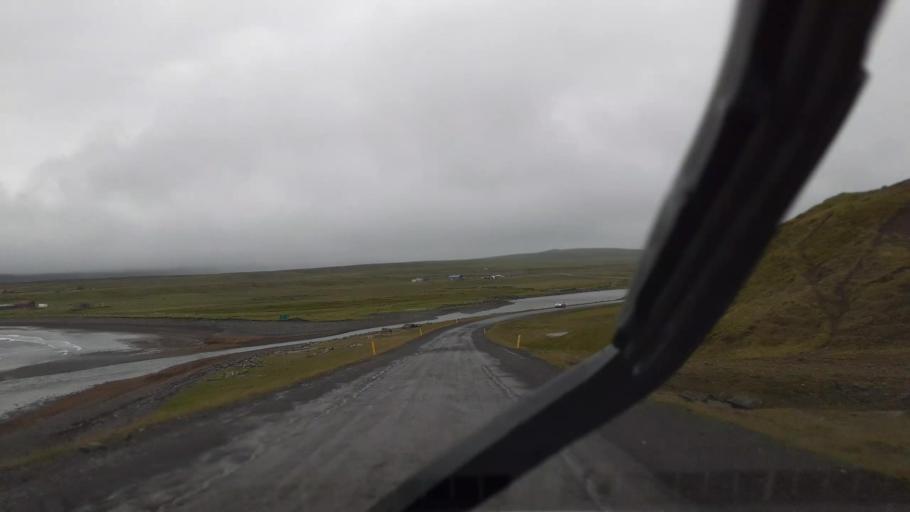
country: IS
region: East
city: Egilsstadir
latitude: 66.0450
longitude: -15.0950
